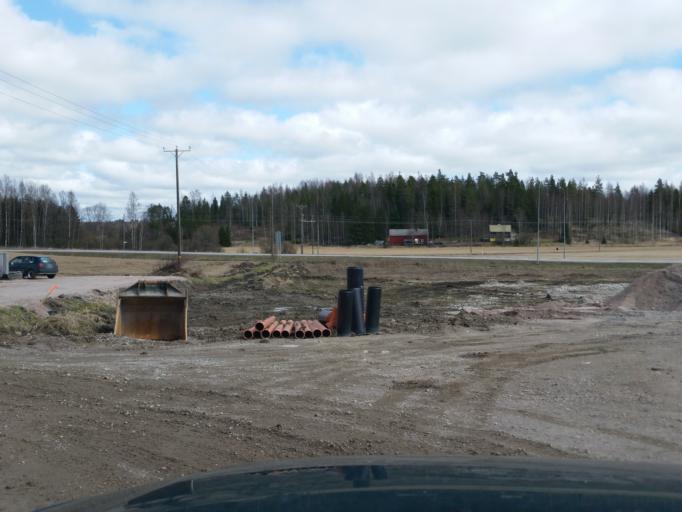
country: FI
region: Uusimaa
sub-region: Helsinki
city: Vihti
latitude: 60.3986
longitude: 24.3302
